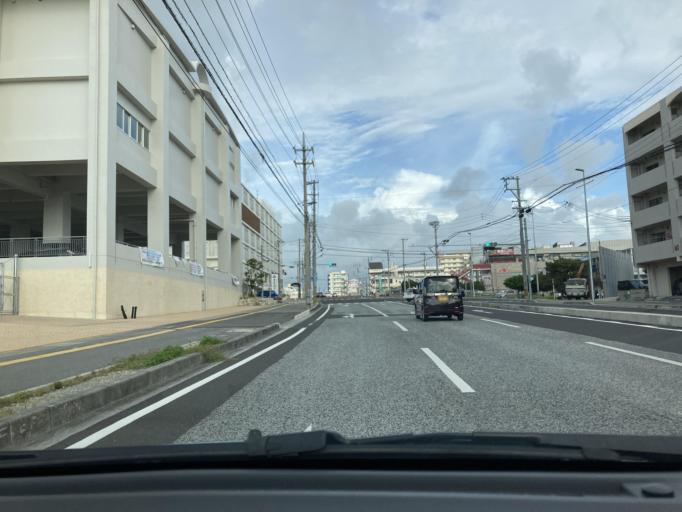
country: JP
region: Okinawa
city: Tomigusuku
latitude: 26.1768
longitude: 127.6798
